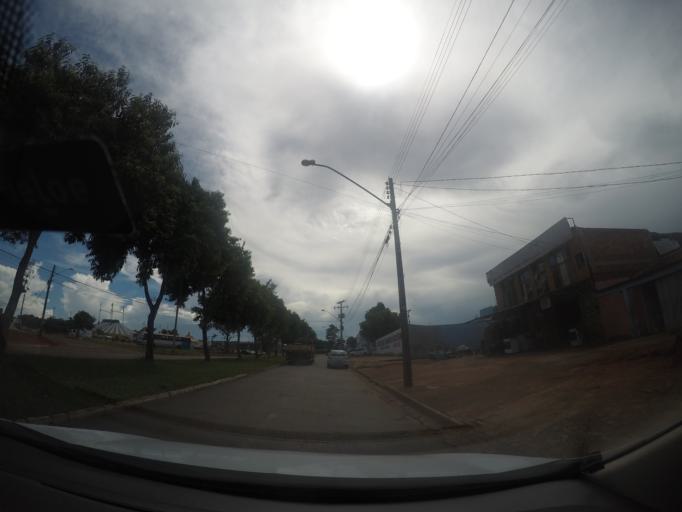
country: BR
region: Goias
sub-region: Trindade
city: Trindade
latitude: -16.6844
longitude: -49.3844
